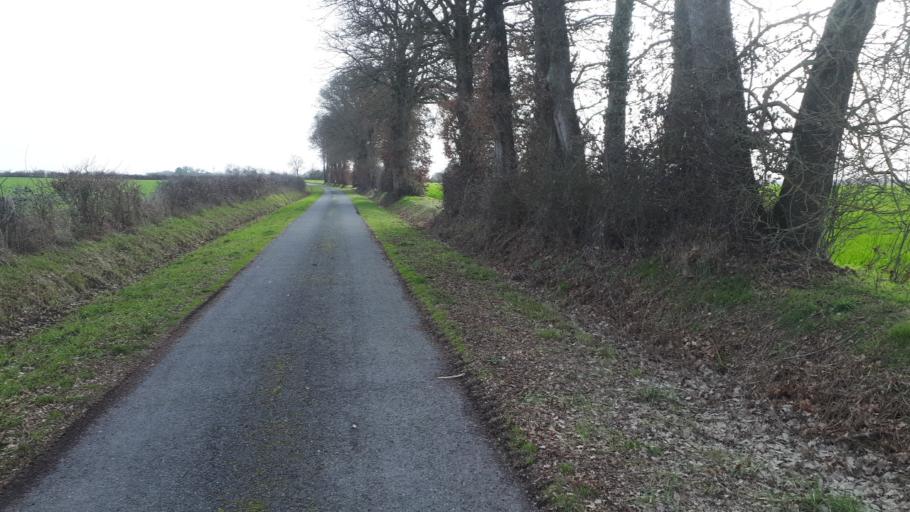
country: FR
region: Poitou-Charentes
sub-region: Departement de la Vienne
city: Archigny
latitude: 46.6320
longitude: 0.7470
